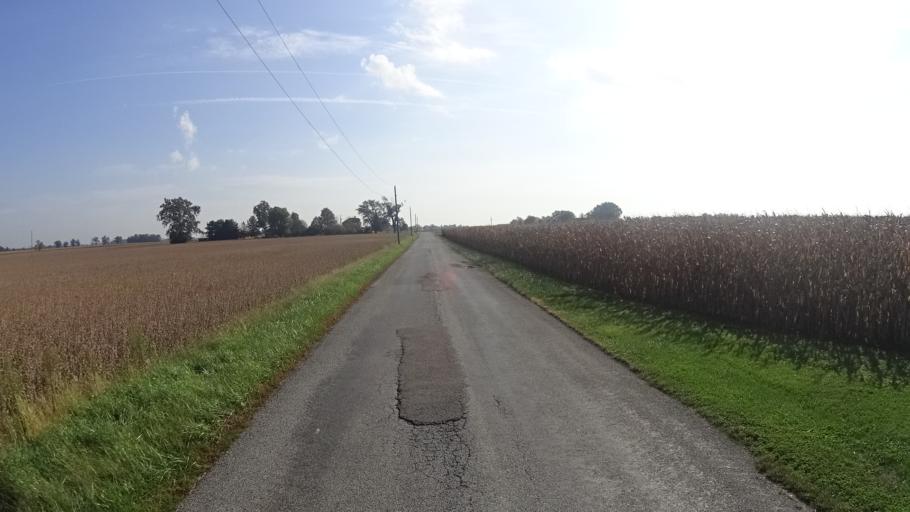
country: US
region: Indiana
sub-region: Madison County
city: Lapel
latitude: 40.0458
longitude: -85.8172
